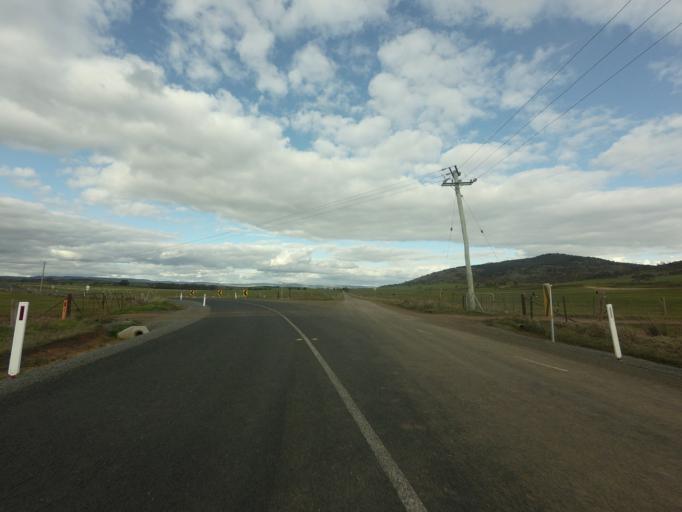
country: AU
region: Tasmania
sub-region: Northern Midlands
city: Evandale
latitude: -41.9124
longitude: 147.3767
